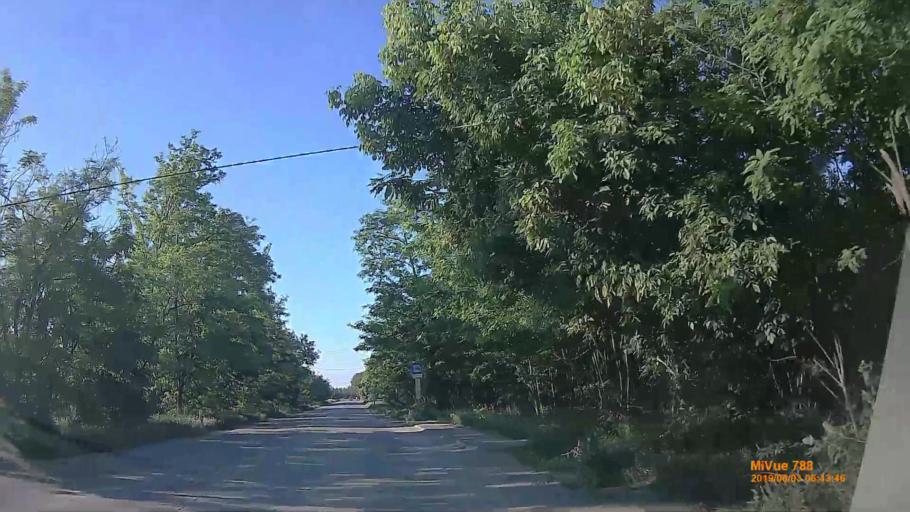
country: HU
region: Pest
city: Bugyi
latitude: 47.2514
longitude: 19.1270
